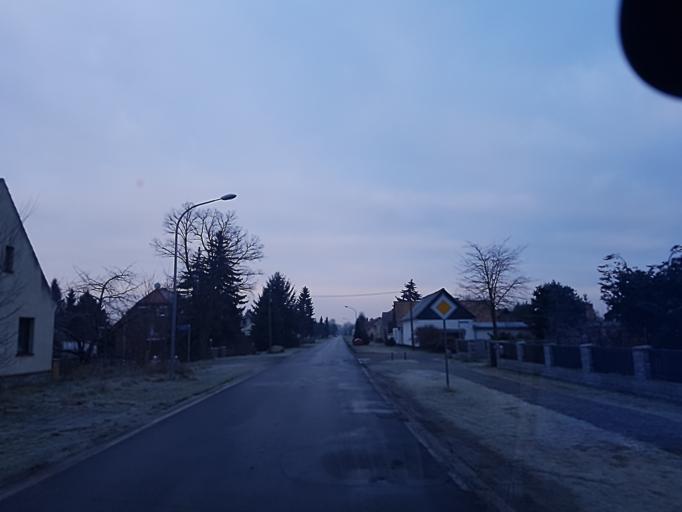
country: DE
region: Brandenburg
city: Finsterwalde
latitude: 51.6582
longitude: 13.7119
